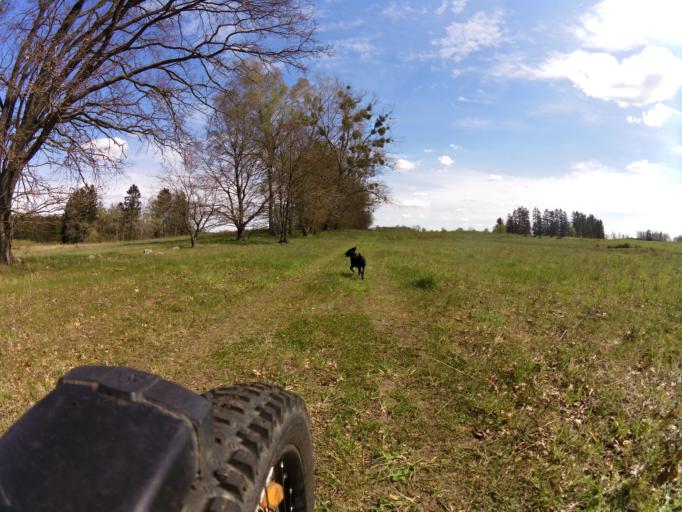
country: PL
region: West Pomeranian Voivodeship
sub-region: Powiat lobeski
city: Resko
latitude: 53.8066
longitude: 15.4573
